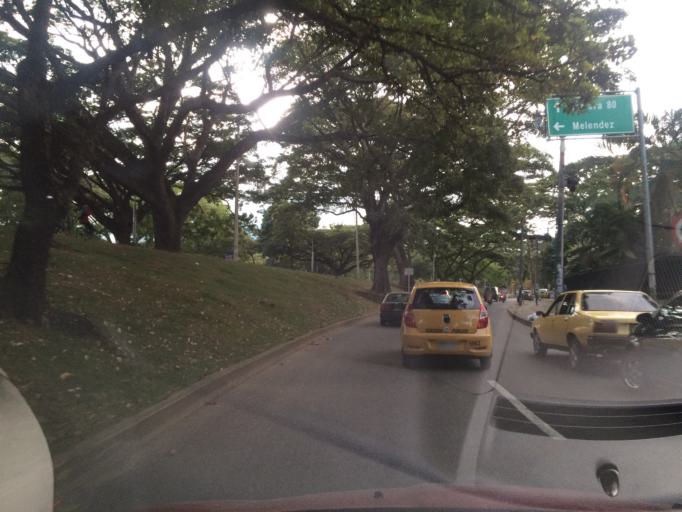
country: CO
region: Valle del Cauca
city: Cali
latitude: 3.3733
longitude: -76.5409
